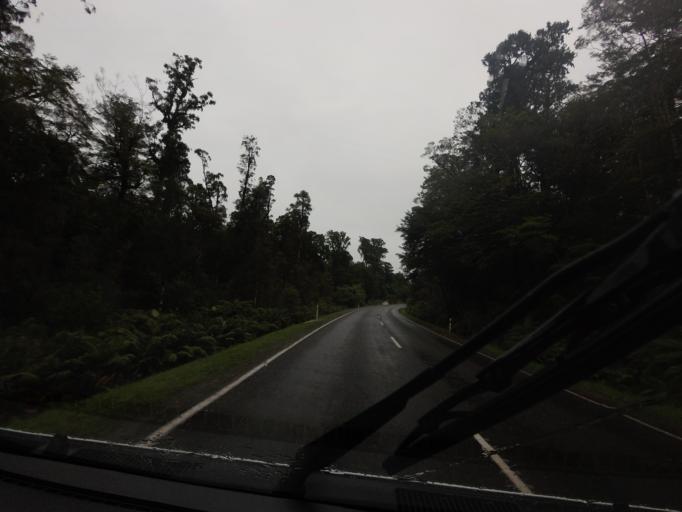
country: NZ
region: Otago
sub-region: Queenstown-Lakes District
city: Wanaka
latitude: -43.8525
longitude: 169.0581
